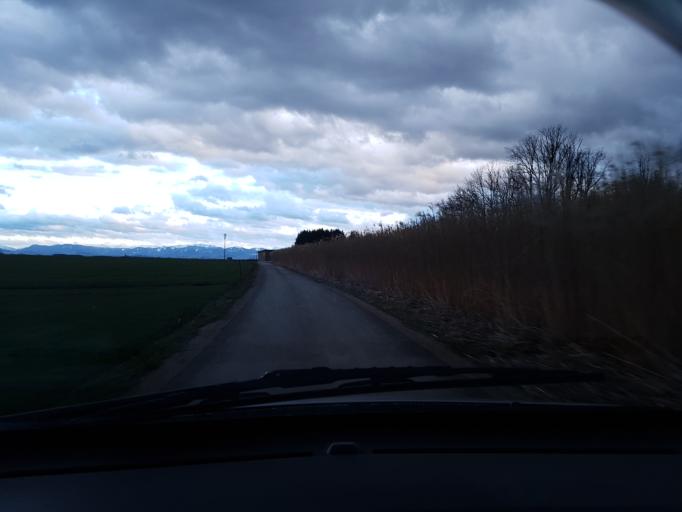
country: AT
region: Upper Austria
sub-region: Politischer Bezirk Linz-Land
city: Ansfelden
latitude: 48.1624
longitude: 14.3184
